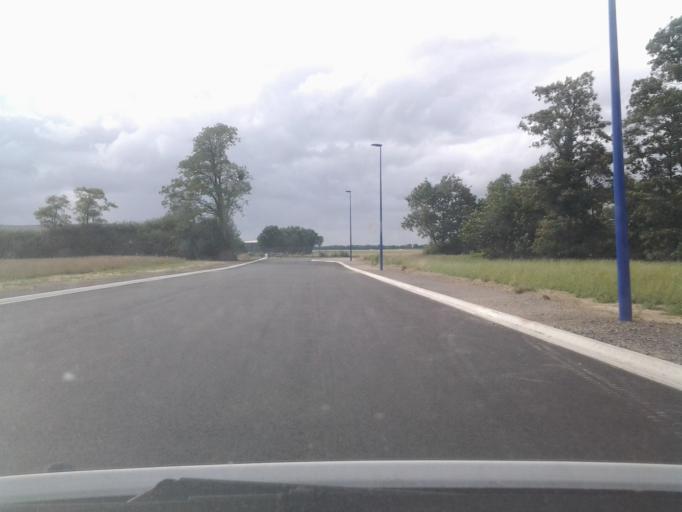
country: FR
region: Pays de la Loire
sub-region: Departement de la Vendee
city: Dompierre-sur-Yon
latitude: 46.6968
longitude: -1.3680
